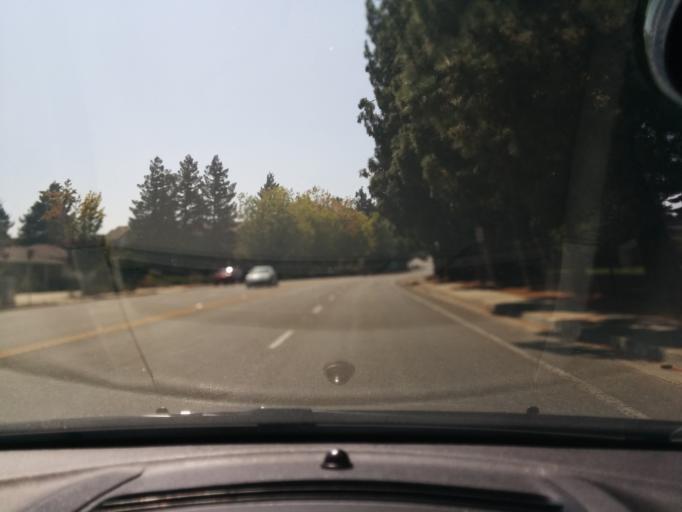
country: US
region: California
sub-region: Santa Clara County
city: Mountain View
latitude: 37.3934
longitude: -122.0611
